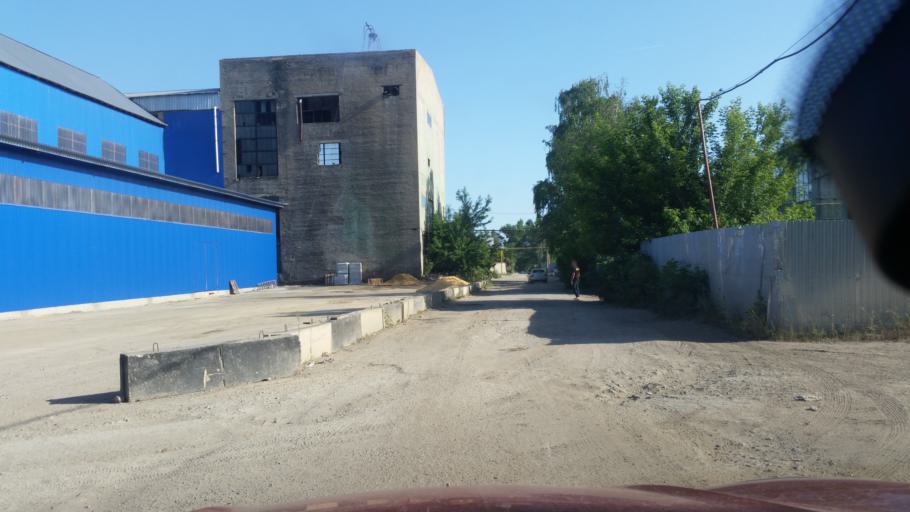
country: RU
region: Orjol
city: Znamenka
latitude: 52.9208
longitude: 35.9867
